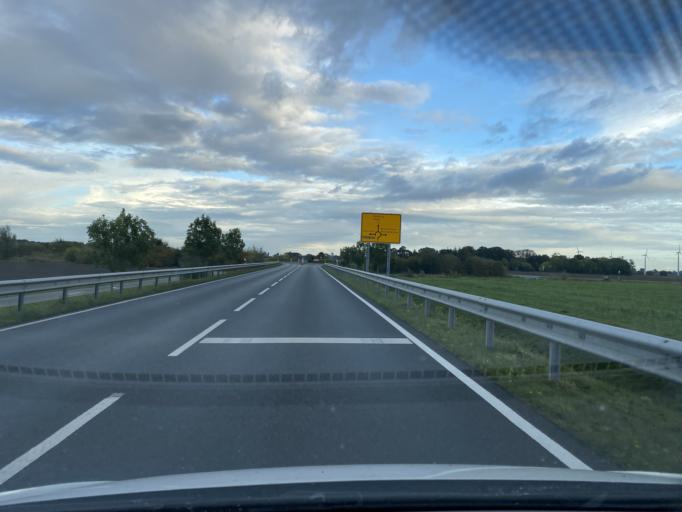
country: DE
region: Lower Saxony
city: Otterndorf
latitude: 53.7961
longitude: 8.8903
